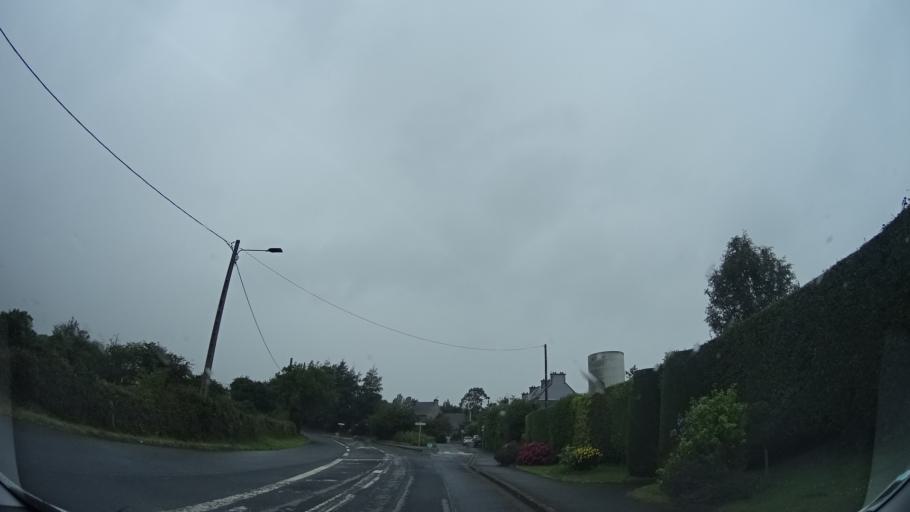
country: FR
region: Lower Normandy
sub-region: Departement de la Manche
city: Octeville
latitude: 49.6210
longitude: -1.6600
